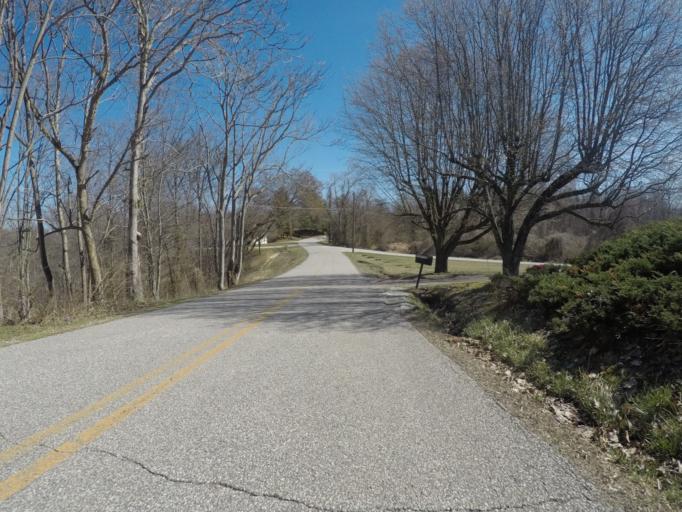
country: US
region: West Virginia
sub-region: Cabell County
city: Huntington
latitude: 38.4432
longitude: -82.4858
